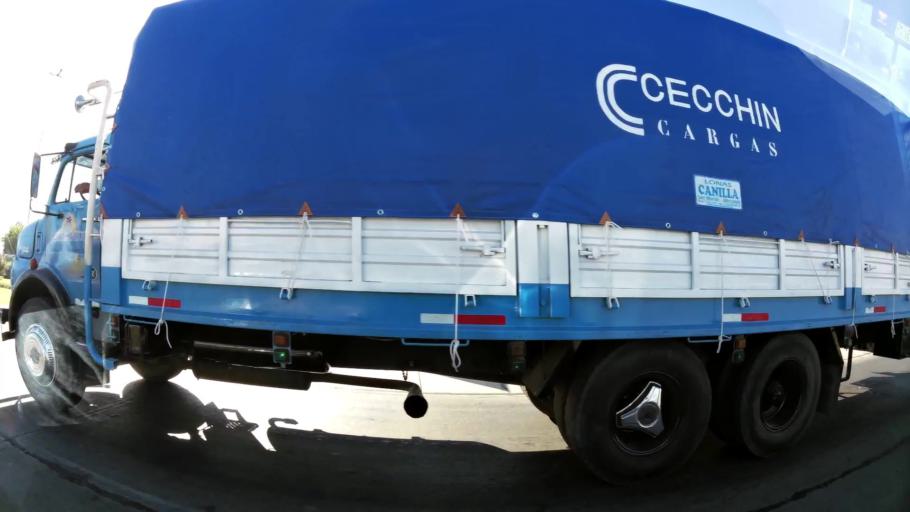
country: AR
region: Mendoza
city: Las Heras
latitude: -32.8280
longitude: -68.8048
